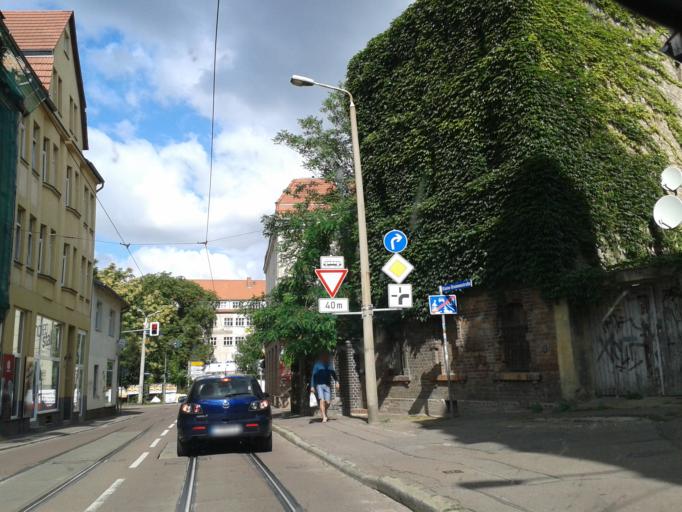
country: DE
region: Saxony-Anhalt
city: Sennewitz
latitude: 51.5006
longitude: 11.9554
